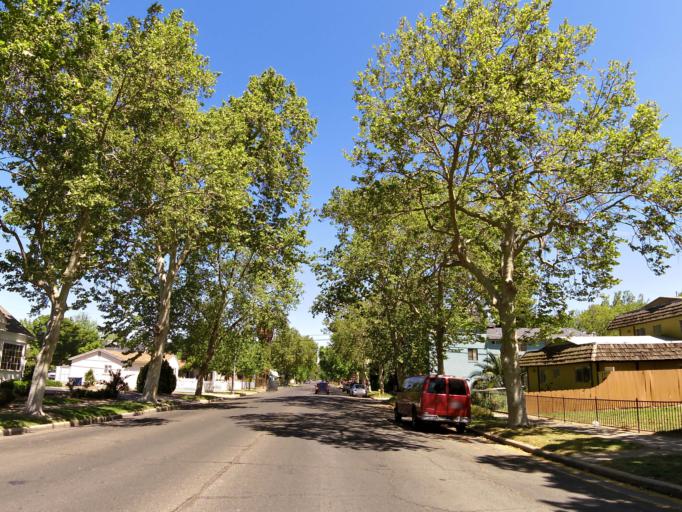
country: US
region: California
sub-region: Merced County
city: Merced
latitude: 37.3039
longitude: -120.4801
